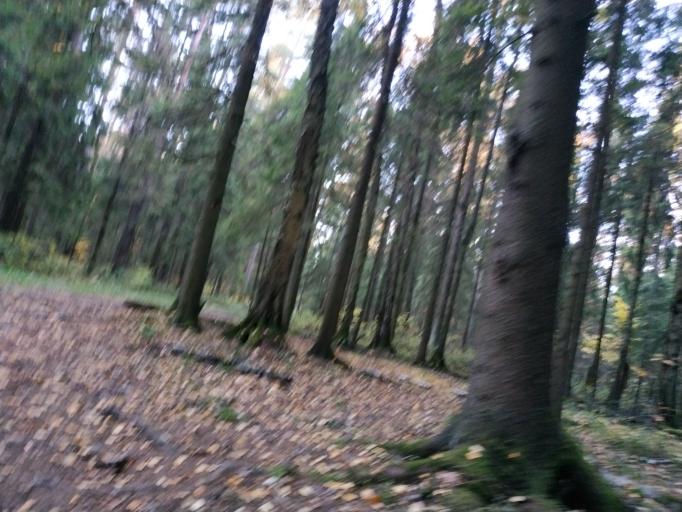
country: RU
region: Moskovskaya
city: Lobnya
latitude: 55.9944
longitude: 37.4688
